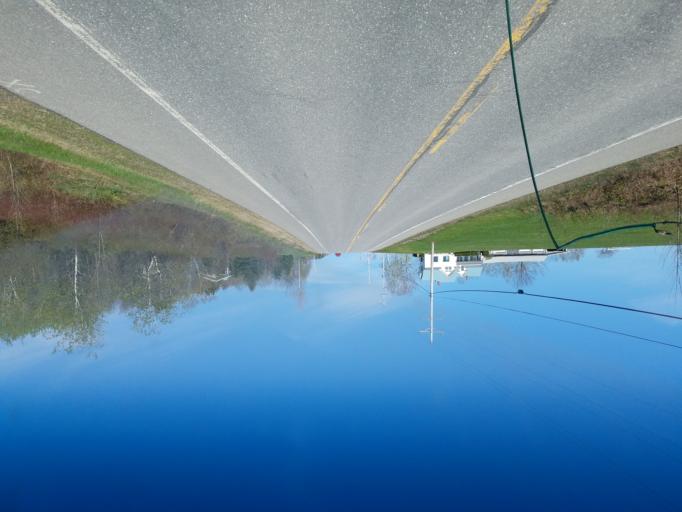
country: US
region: Maine
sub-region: Aroostook County
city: Presque Isle
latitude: 46.6667
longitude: -68.2090
